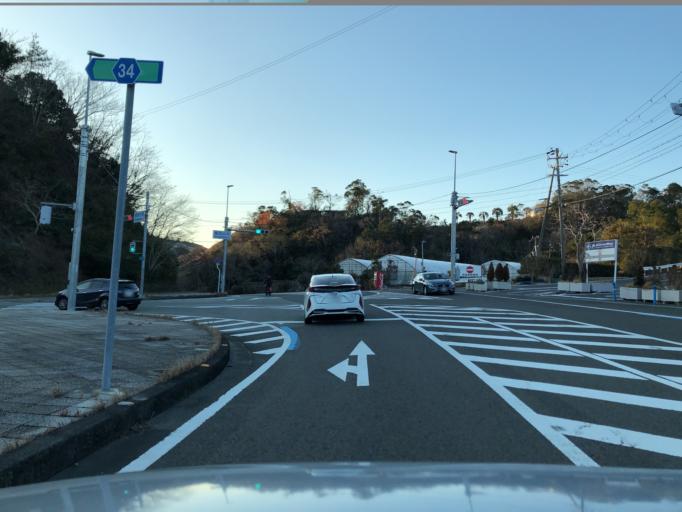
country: JP
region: Wakayama
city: Tanabe
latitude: 33.6627
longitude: 135.3739
